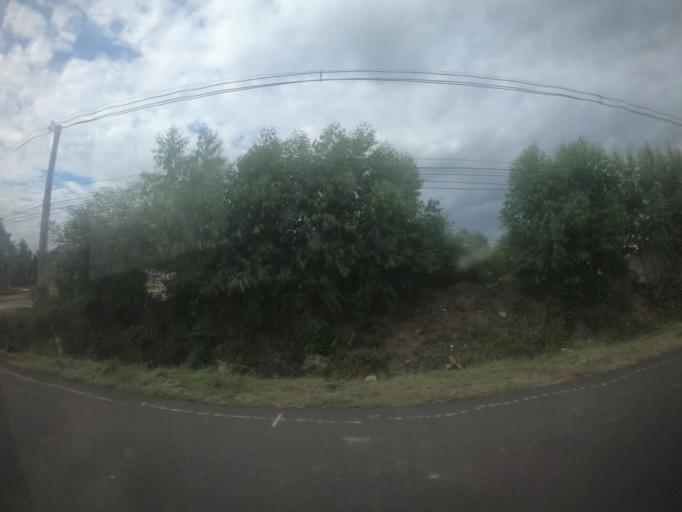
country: TH
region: Surin
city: Prasat
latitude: 14.5621
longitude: 103.4972
